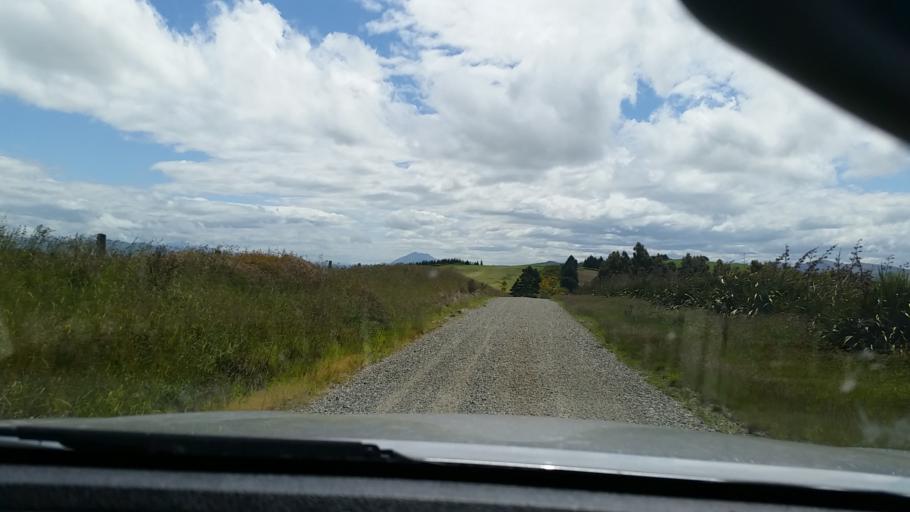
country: NZ
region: Southland
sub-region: Southland District
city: Winton
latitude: -45.7925
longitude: 168.5420
